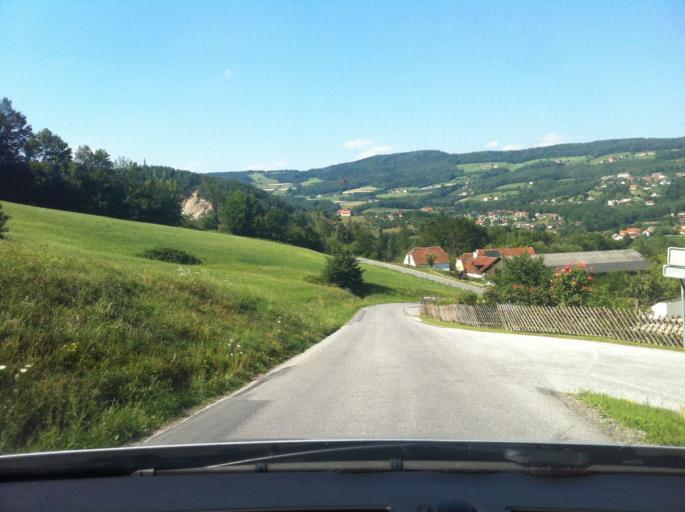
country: AT
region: Styria
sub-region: Politischer Bezirk Hartberg-Fuerstenfeld
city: Stubenberg
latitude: 47.2360
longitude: 15.7894
